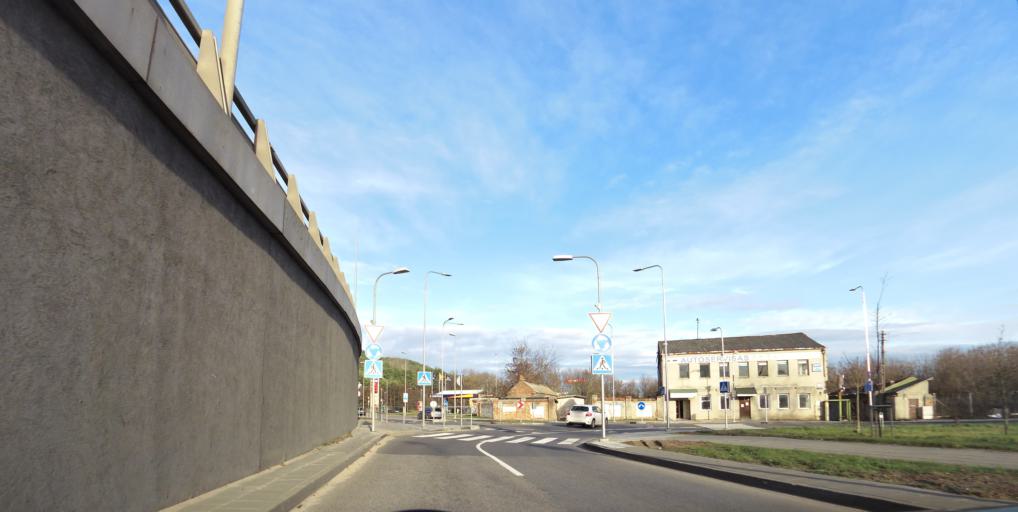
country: LT
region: Vilnius County
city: Seskine
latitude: 54.7011
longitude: 25.2645
